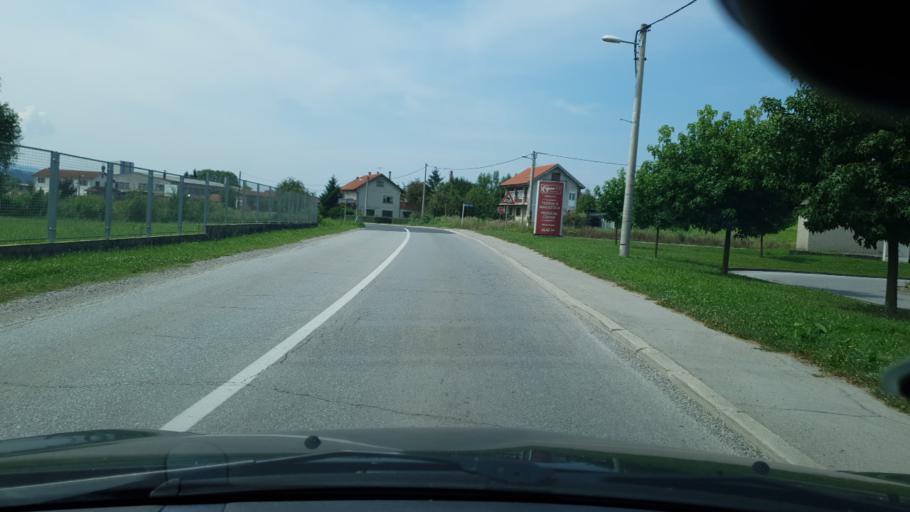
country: HR
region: Krapinsko-Zagorska
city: Bedekovcina
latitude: 46.0442
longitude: 16.0031
